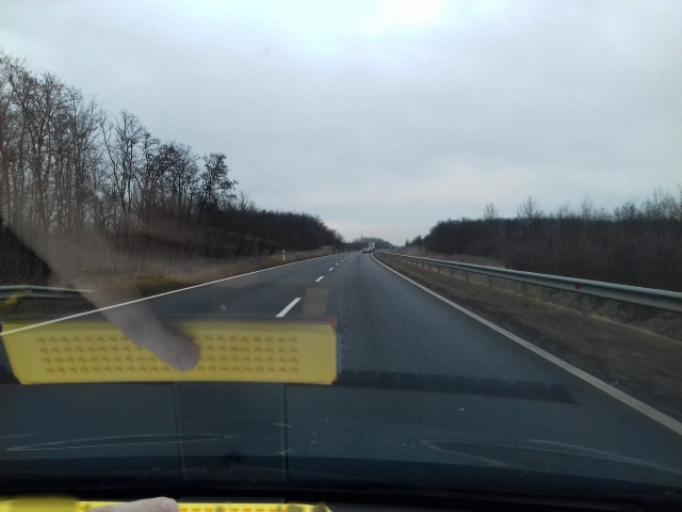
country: HU
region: Szabolcs-Szatmar-Bereg
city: Napkor
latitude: 47.9248
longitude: 21.8199
